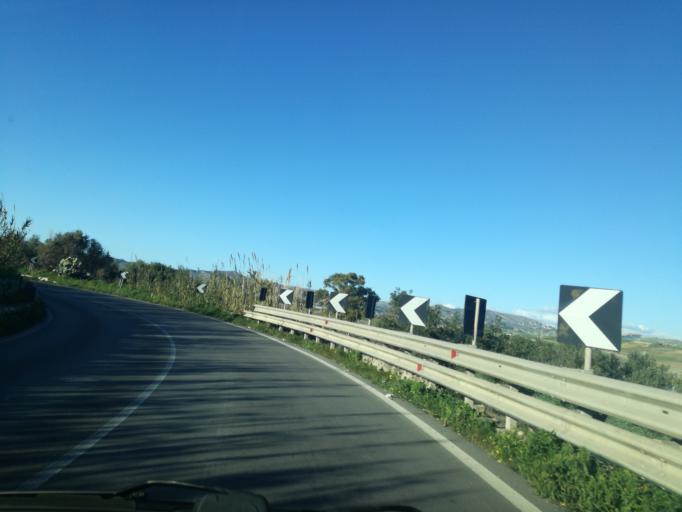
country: IT
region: Sicily
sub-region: Provincia di Caltanissetta
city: Butera
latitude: 37.1128
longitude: 14.1549
